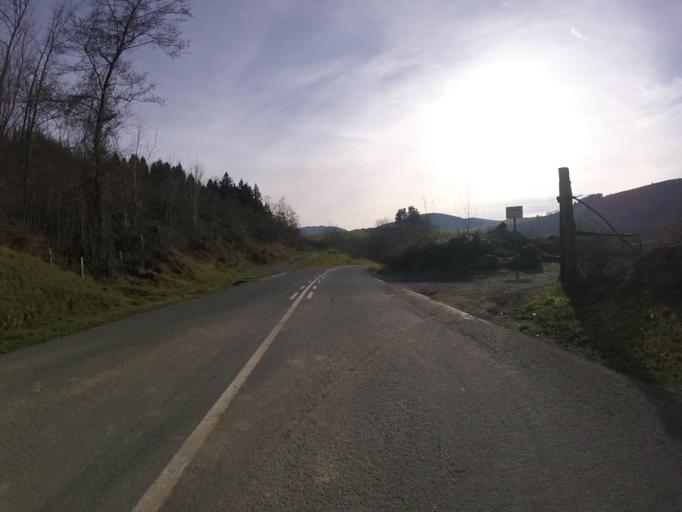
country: ES
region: Navarre
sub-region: Provincia de Navarra
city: Areso
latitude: 43.1021
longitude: -1.9536
